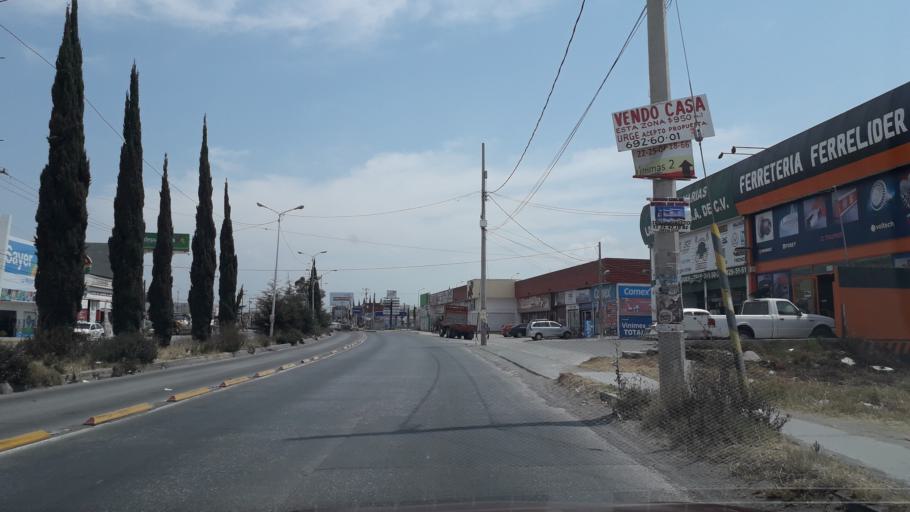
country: MX
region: Puebla
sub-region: Puebla
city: El Capulo (La Quebradora)
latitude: 18.9759
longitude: -98.2574
